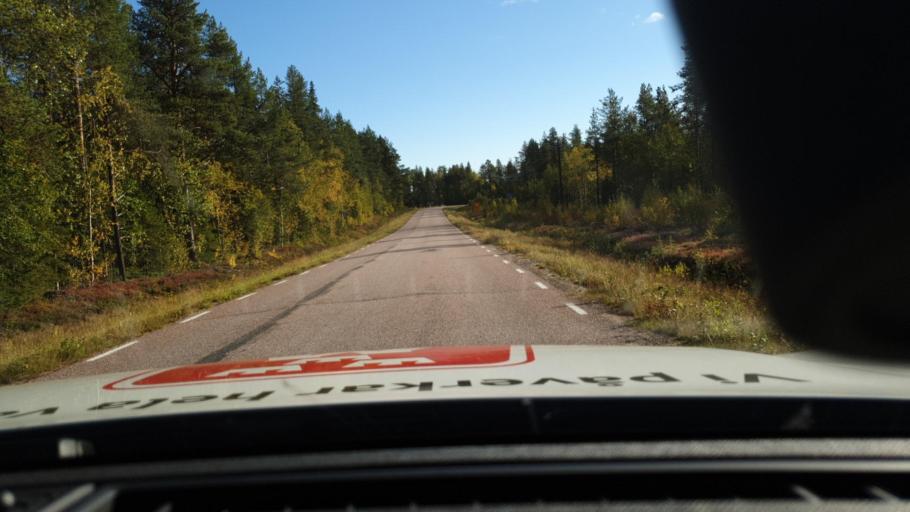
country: SE
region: Norrbotten
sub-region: Pajala Kommun
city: Pajala
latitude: 67.1948
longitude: 23.3349
